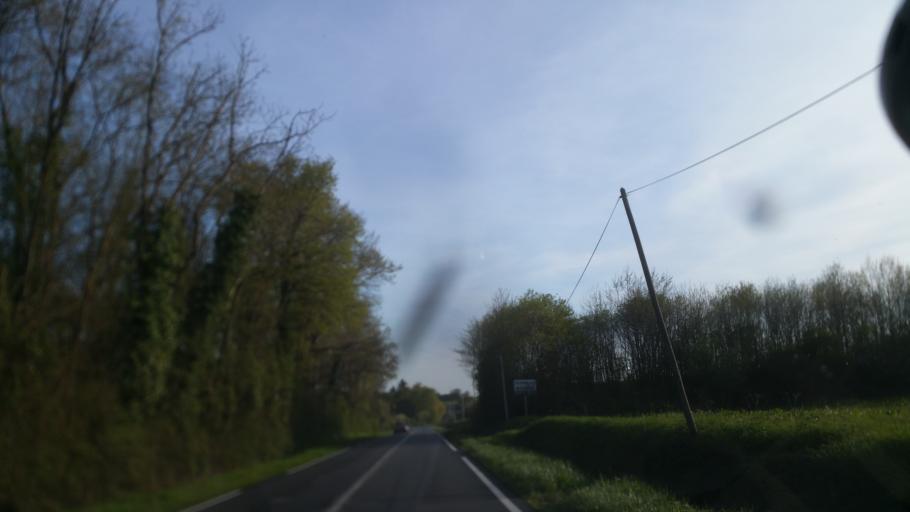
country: FR
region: Ile-de-France
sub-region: Departement de l'Essonne
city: Dourdan
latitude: 48.5476
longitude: 2.0205
